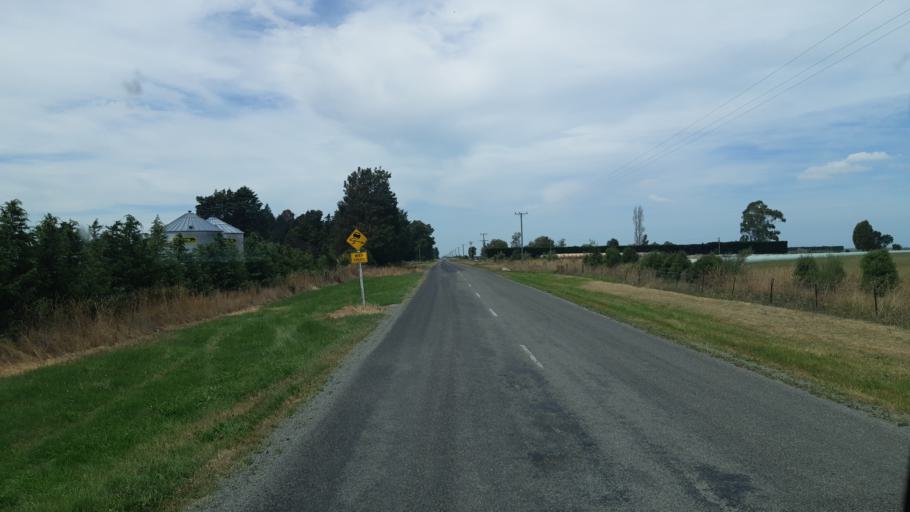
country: NZ
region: Canterbury
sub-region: Ashburton District
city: Tinwald
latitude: -43.9207
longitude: 171.5350
